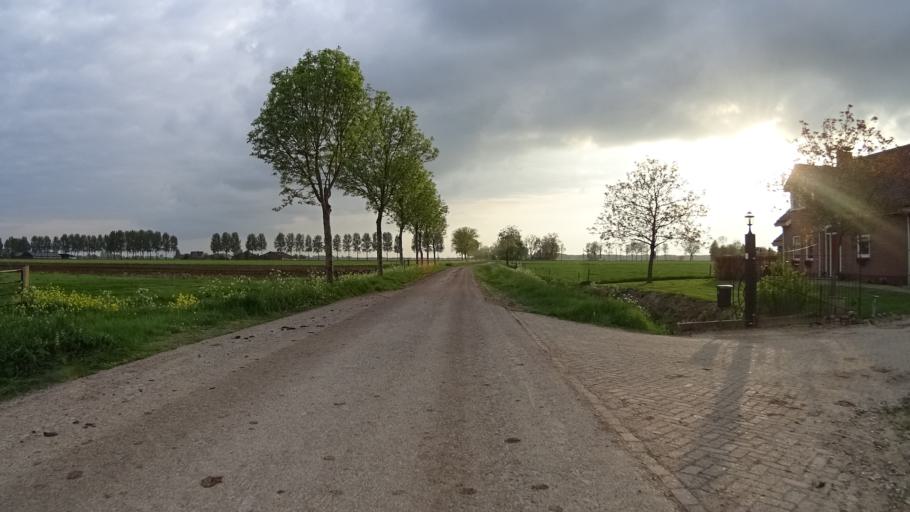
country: NL
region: North Brabant
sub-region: Gemeente Aalburg
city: Aalburg
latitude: 51.7644
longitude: 5.0821
